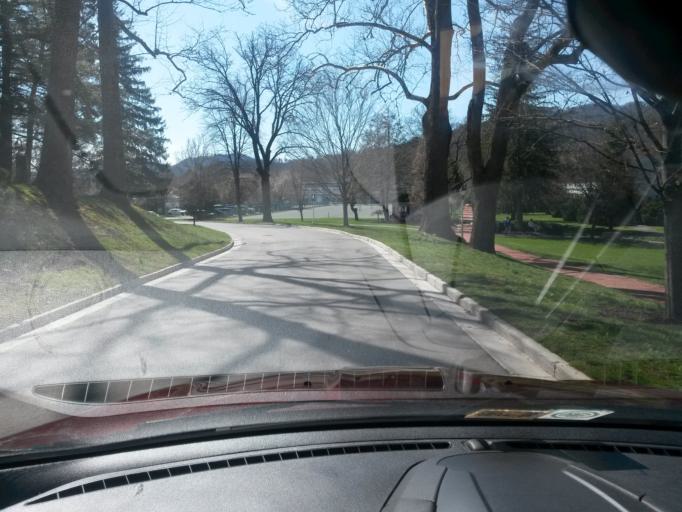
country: US
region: West Virginia
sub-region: Greenbrier County
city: White Sulphur Springs
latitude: 37.7874
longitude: -80.3121
